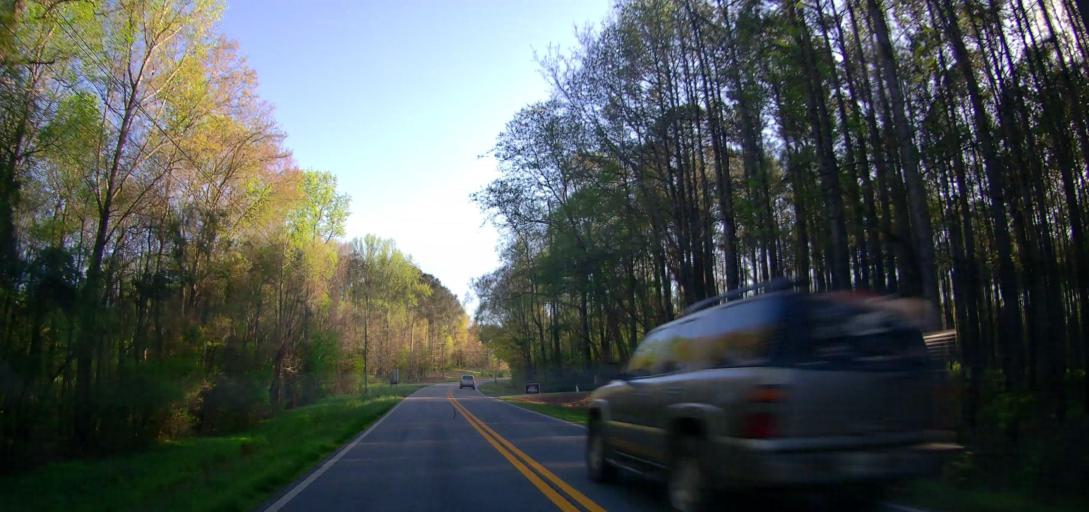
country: US
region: Georgia
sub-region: Butts County
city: Jackson
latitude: 33.3096
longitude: -83.9039
